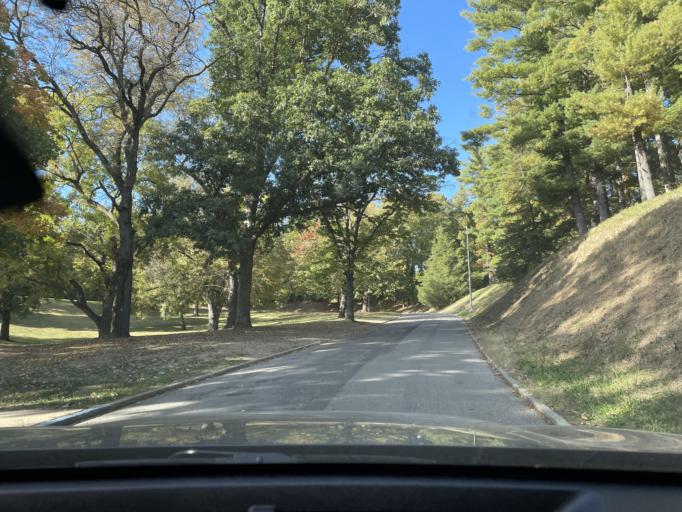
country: US
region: Missouri
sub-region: Buchanan County
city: Saint Joseph
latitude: 39.8002
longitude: -94.8506
